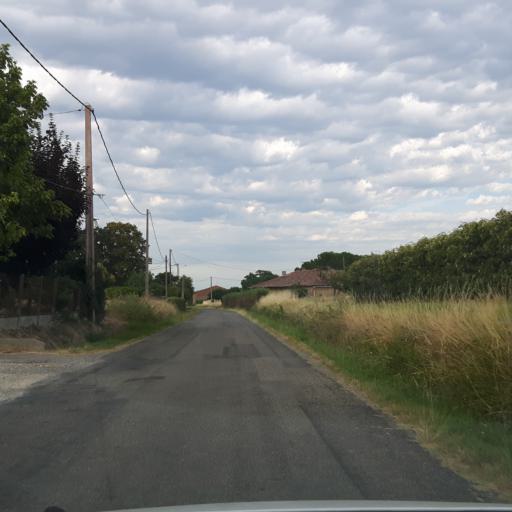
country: FR
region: Midi-Pyrenees
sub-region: Departement de la Haute-Garonne
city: Fronton
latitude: 43.8248
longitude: 1.3687
